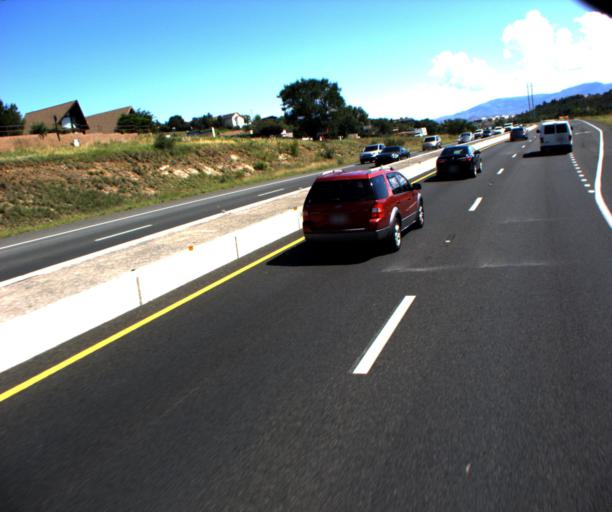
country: US
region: Arizona
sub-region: Yavapai County
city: Prescott Valley
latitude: 34.5606
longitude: -112.3786
